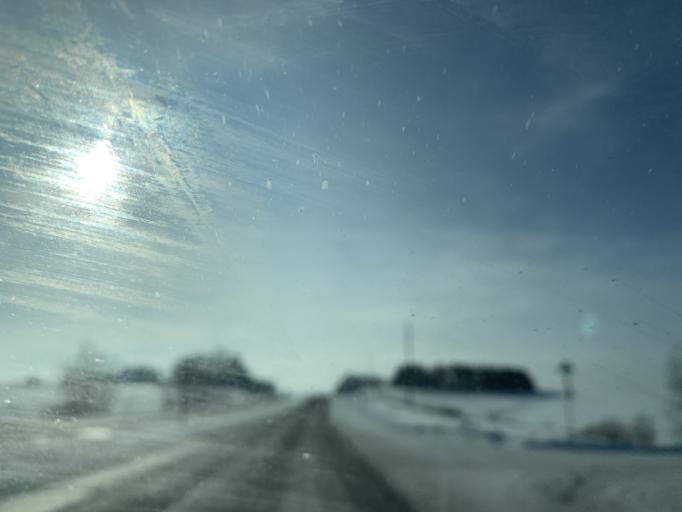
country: US
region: Minnesota
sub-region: Dakota County
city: Lakeville
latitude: 44.6743
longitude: -93.2172
